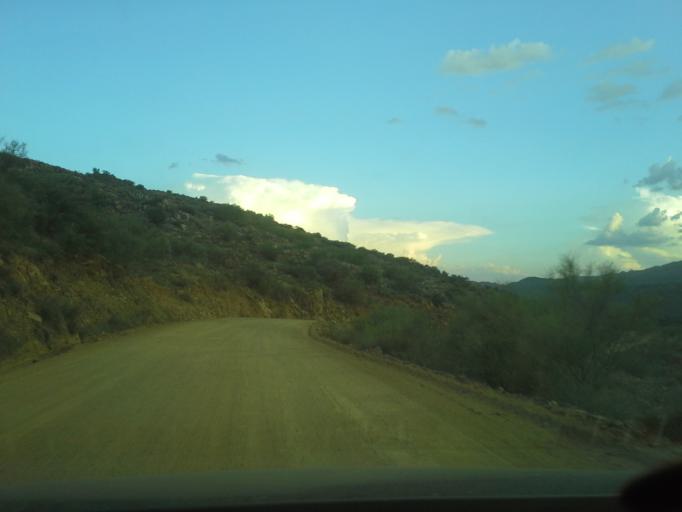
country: US
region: Arizona
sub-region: Yavapai County
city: Black Canyon City
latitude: 34.1765
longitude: -112.1654
